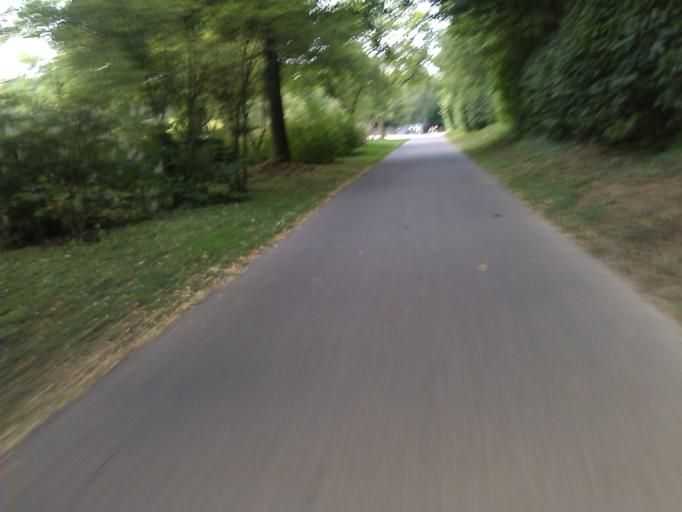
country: DE
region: Baden-Wuerttemberg
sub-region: Regierungsbezirk Stuttgart
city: Heilbronn
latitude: 49.1291
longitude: 9.2037
